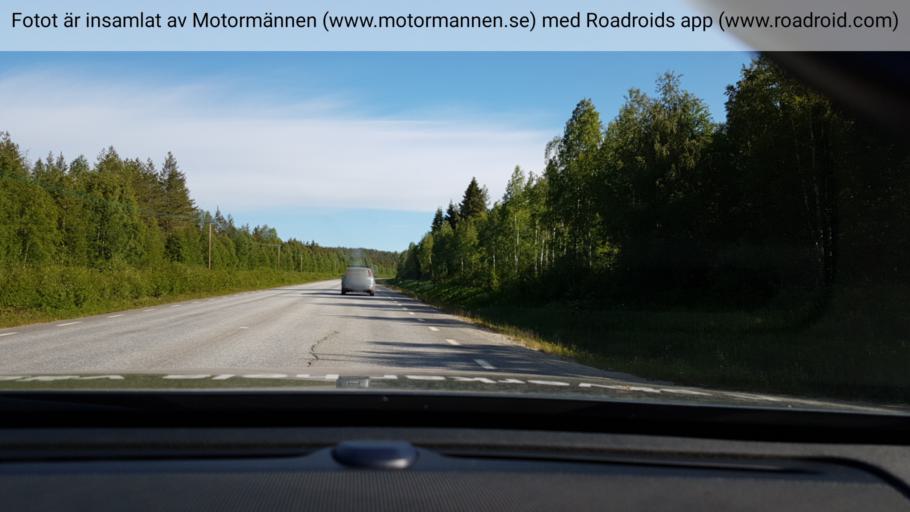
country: SE
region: Vaesterbotten
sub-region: Vannas Kommun
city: Vaennaes
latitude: 64.0178
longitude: 19.6931
